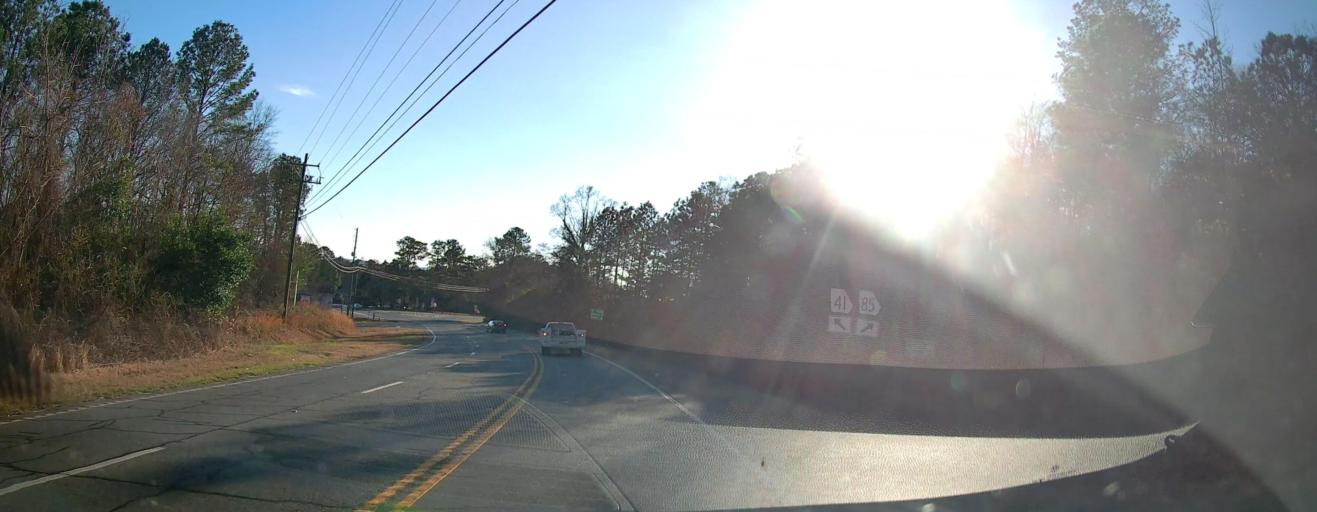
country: US
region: Georgia
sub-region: Meriwether County
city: Manchester
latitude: 32.8432
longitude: -84.6227
